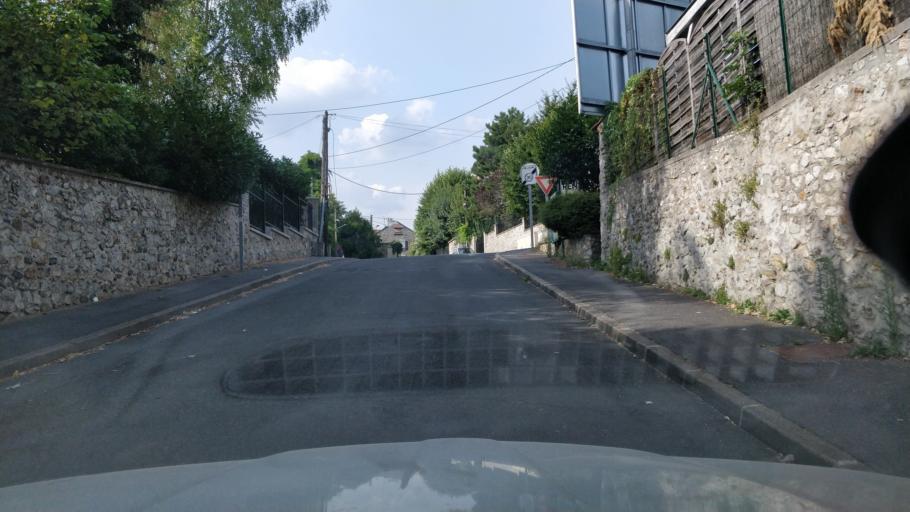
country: FR
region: Ile-de-France
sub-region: Departement de Seine-et-Marne
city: Thorigny-sur-Marne
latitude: 48.8854
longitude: 2.7031
